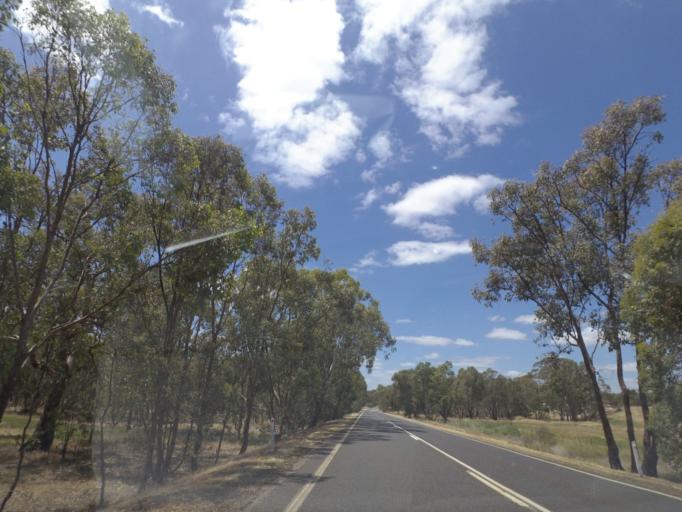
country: AU
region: Victoria
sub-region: Wangaratta
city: Wangaratta
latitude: -36.4657
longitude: 146.2132
